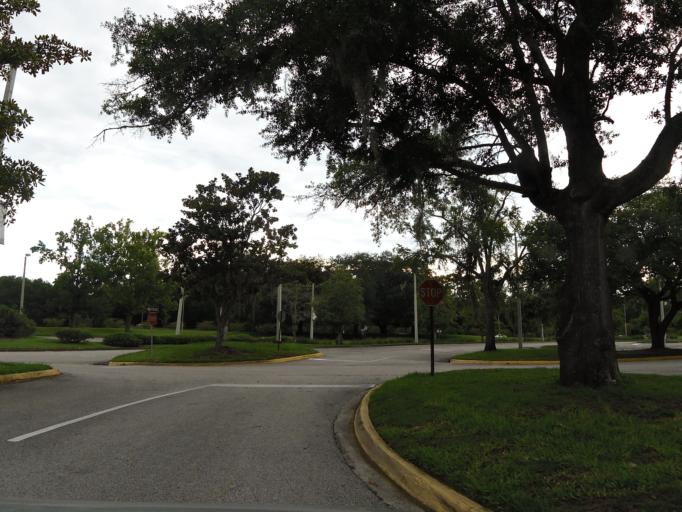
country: US
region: Florida
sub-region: Duval County
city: Jacksonville
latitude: 30.2978
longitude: -81.7188
